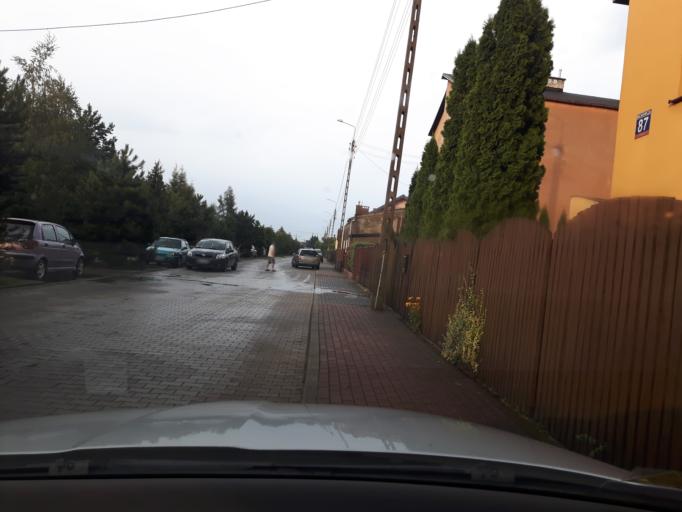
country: PL
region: Masovian Voivodeship
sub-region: Powiat wolominski
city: Zabki
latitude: 52.2899
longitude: 21.0939
